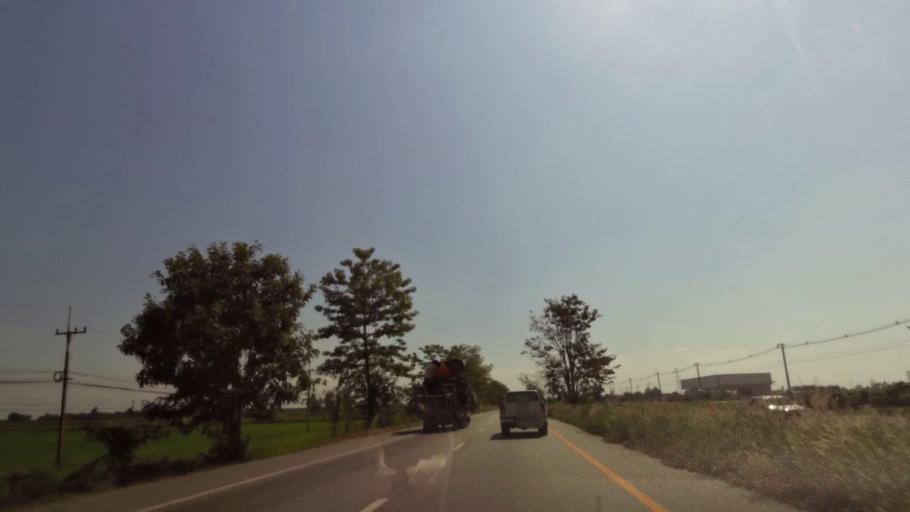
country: TH
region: Nakhon Sawan
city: Kao Liao
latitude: 15.8325
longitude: 100.1182
